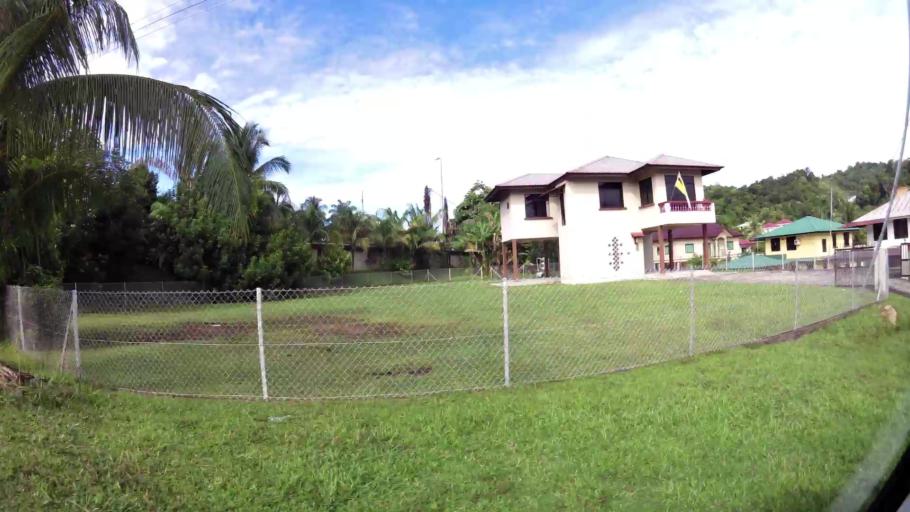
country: BN
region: Brunei and Muara
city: Bandar Seri Begawan
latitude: 4.8955
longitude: 114.9681
